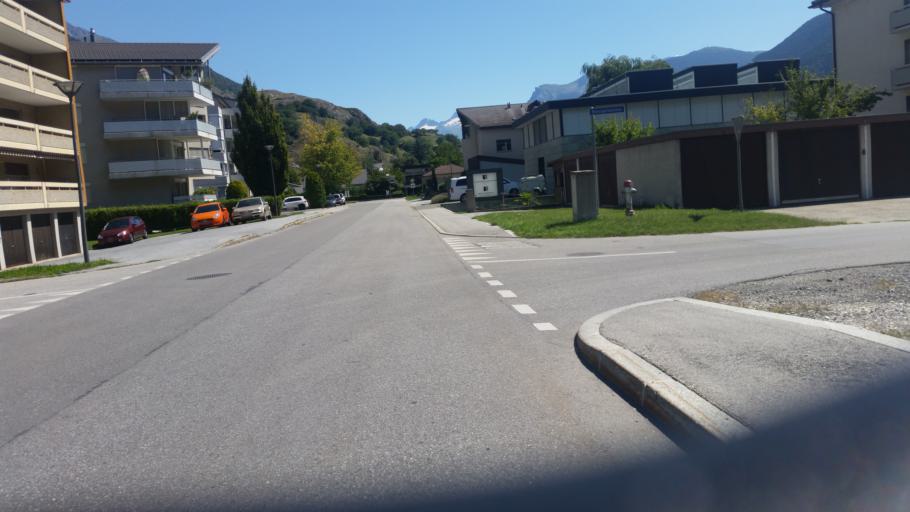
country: CH
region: Valais
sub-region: Raron District
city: Raron
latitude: 46.3090
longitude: 7.7983
